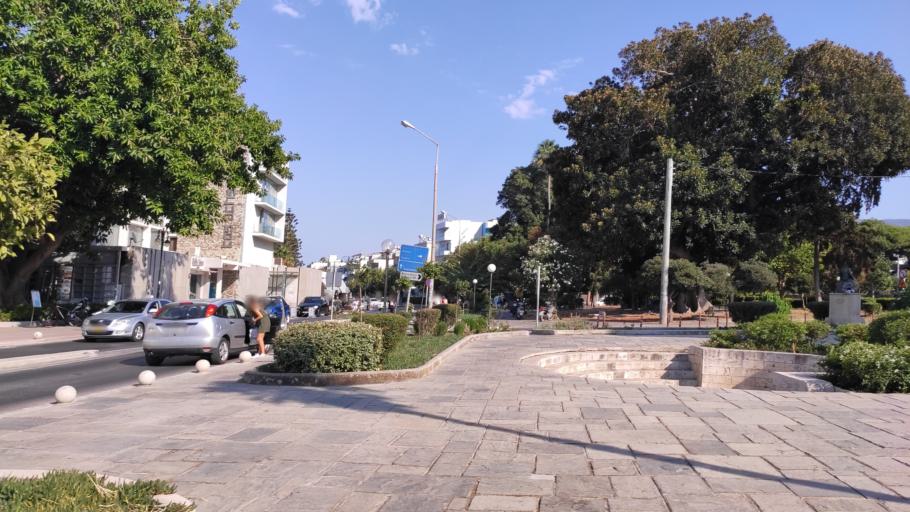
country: GR
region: South Aegean
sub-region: Nomos Dodekanisou
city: Kos
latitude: 36.8933
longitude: 27.2931
